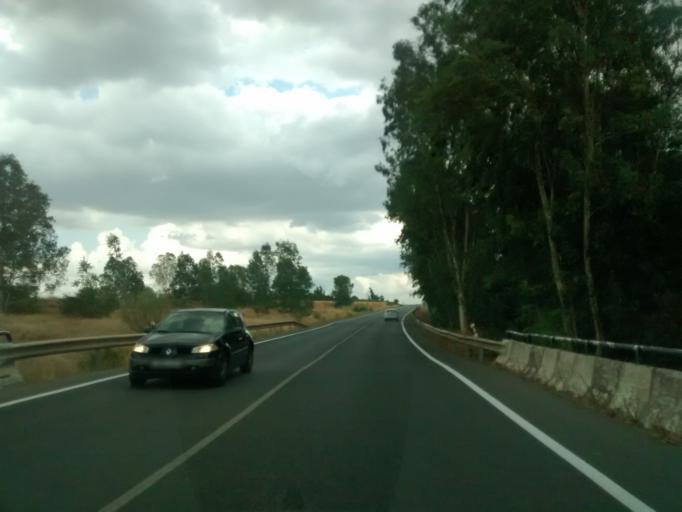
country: ES
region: Andalusia
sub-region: Provincia de Cadiz
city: Villamartin
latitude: 36.8599
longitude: -5.6217
